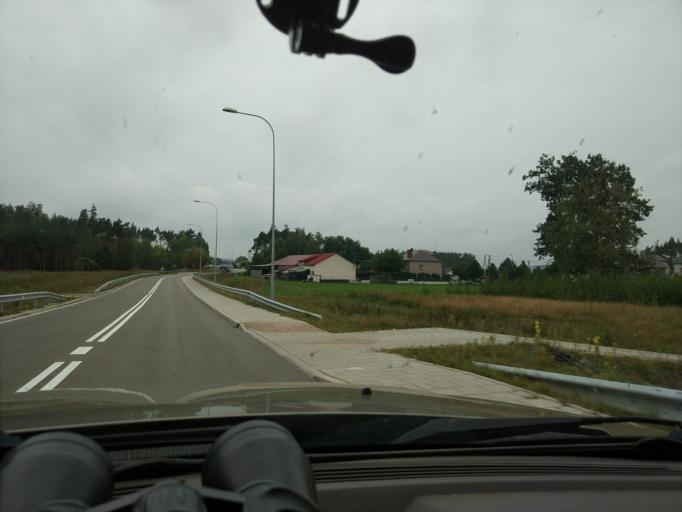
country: PL
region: Podlasie
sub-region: Powiat zambrowski
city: Szumowo
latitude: 52.9131
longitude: 22.0936
